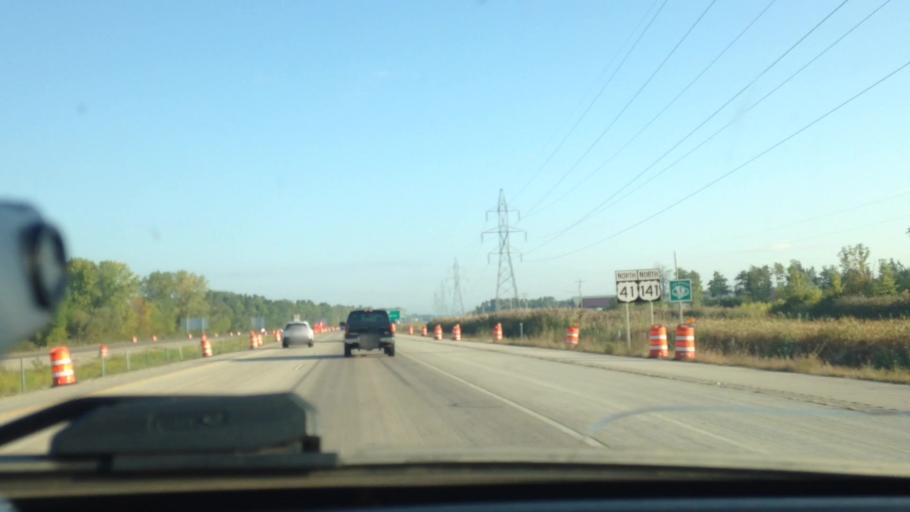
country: US
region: Wisconsin
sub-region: Brown County
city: Suamico
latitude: 44.5977
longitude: -88.0495
